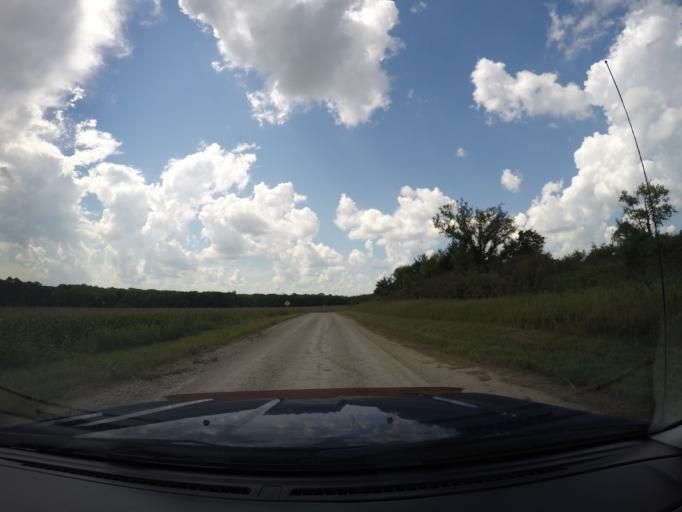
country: US
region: Kansas
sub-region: Wabaunsee County
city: Alma
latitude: 39.0445
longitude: -96.3182
